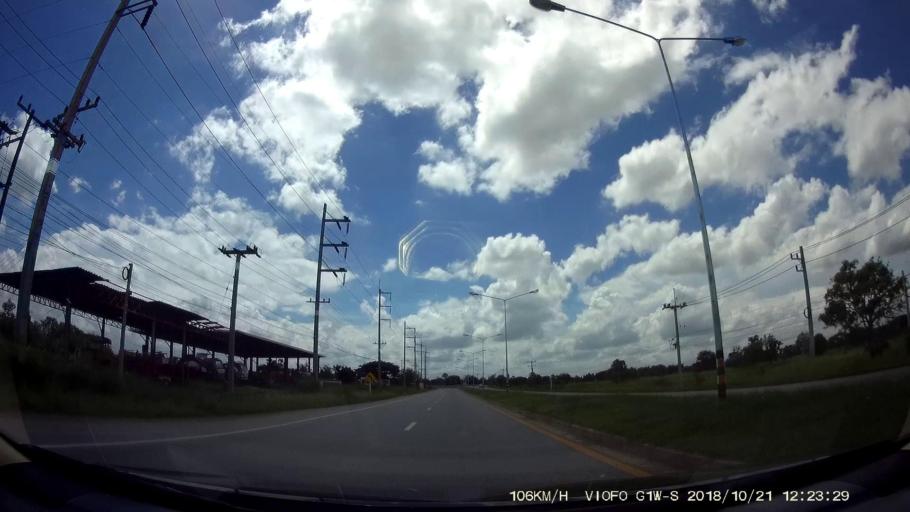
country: TH
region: Nakhon Ratchasima
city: Dan Khun Thot
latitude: 15.2448
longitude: 101.7872
